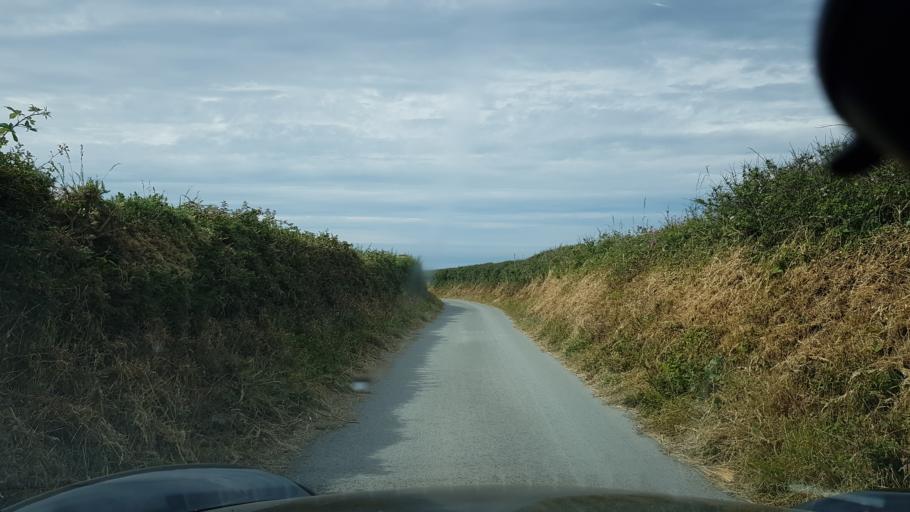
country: GB
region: Wales
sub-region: Pembrokeshire
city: Dale
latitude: 51.7297
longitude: -5.2182
